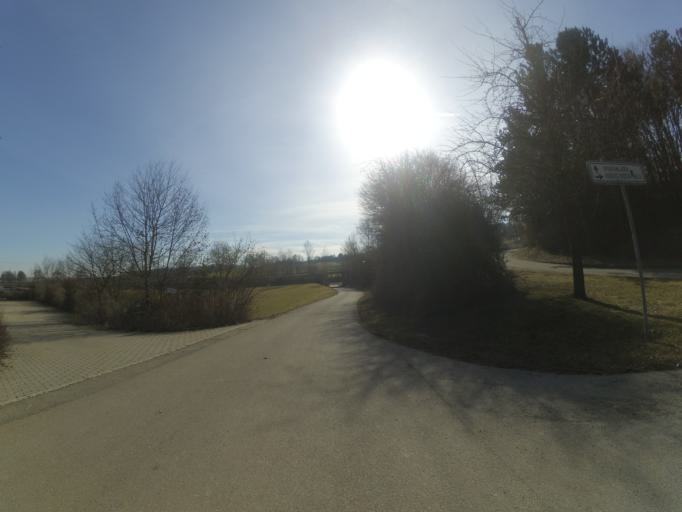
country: DE
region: Baden-Wuerttemberg
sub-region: Tuebingen Region
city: Bernstadt
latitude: 48.4842
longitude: 10.0637
